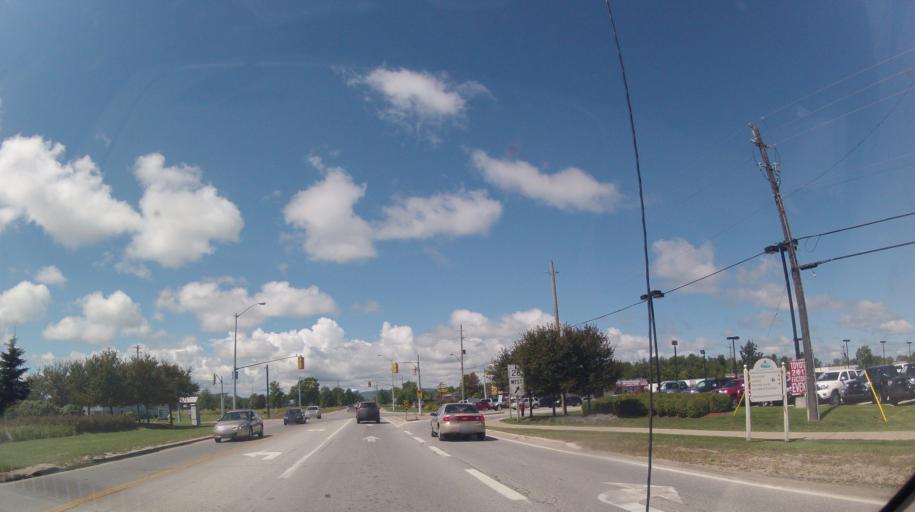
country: CA
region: Ontario
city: Collingwood
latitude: 44.4997
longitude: -80.1948
